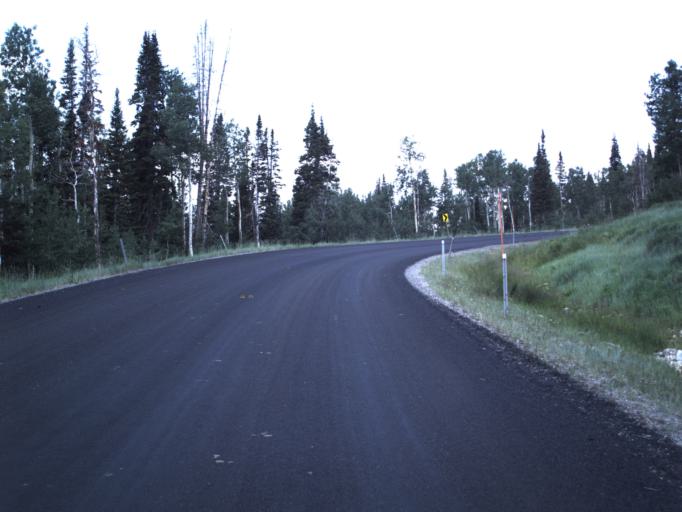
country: US
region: Utah
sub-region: Summit County
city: Francis
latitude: 40.4952
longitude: -111.0366
